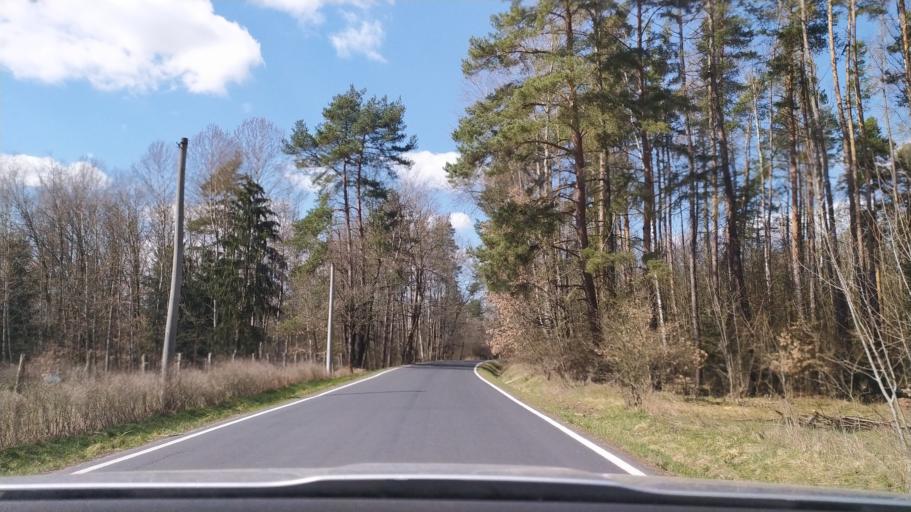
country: CZ
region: Karlovarsky
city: Hazlov
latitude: 50.1116
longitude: 12.2982
